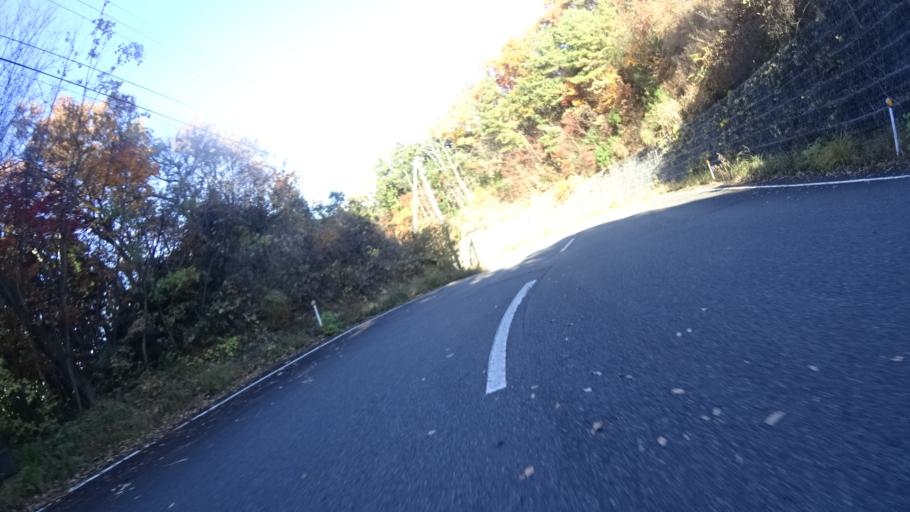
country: JP
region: Niigata
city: Yoshida-kasugacho
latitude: 37.6619
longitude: 138.8135
